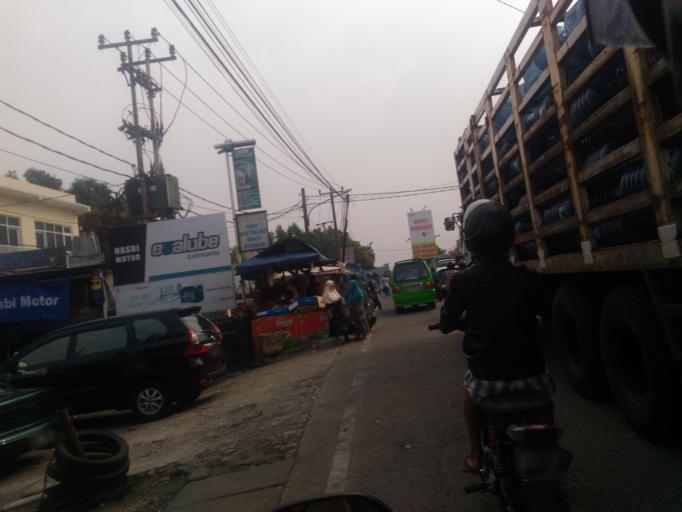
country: ID
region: West Java
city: Caringin
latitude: -6.6567
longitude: 106.8467
